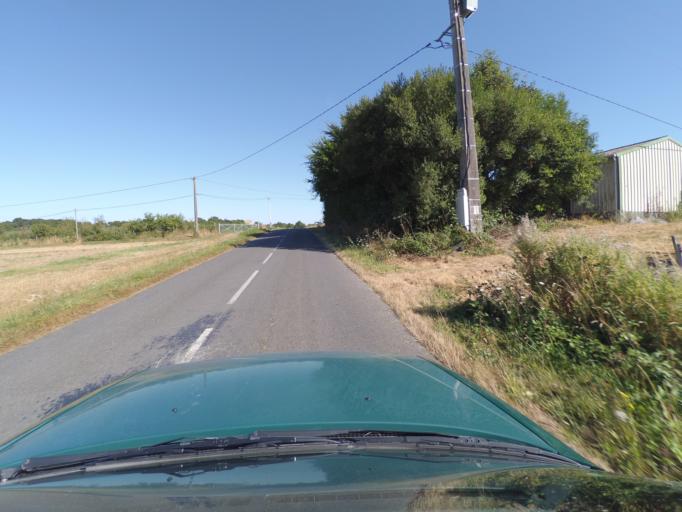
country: FR
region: Pays de la Loire
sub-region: Departement de la Loire-Atlantique
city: Maisdon-sur-Sevre
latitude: 47.1030
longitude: -1.3990
